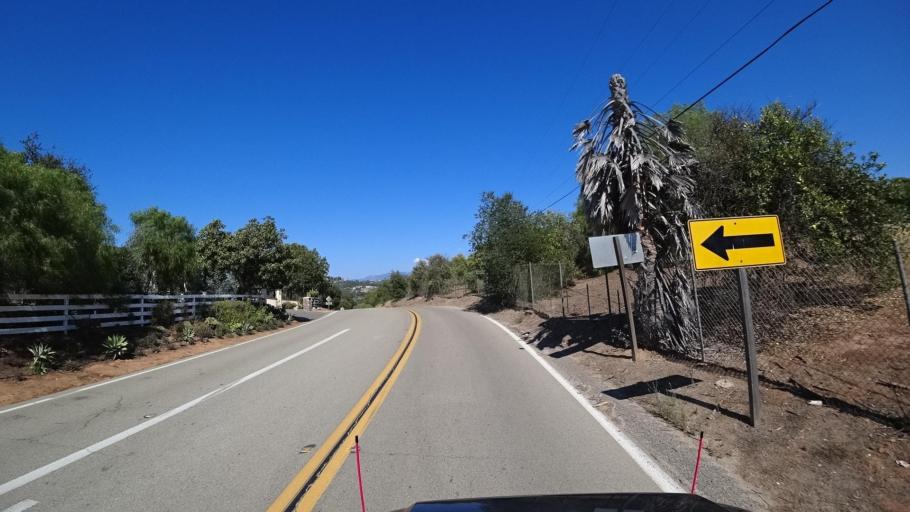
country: US
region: California
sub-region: San Diego County
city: Bonsall
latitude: 33.2963
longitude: -117.1698
